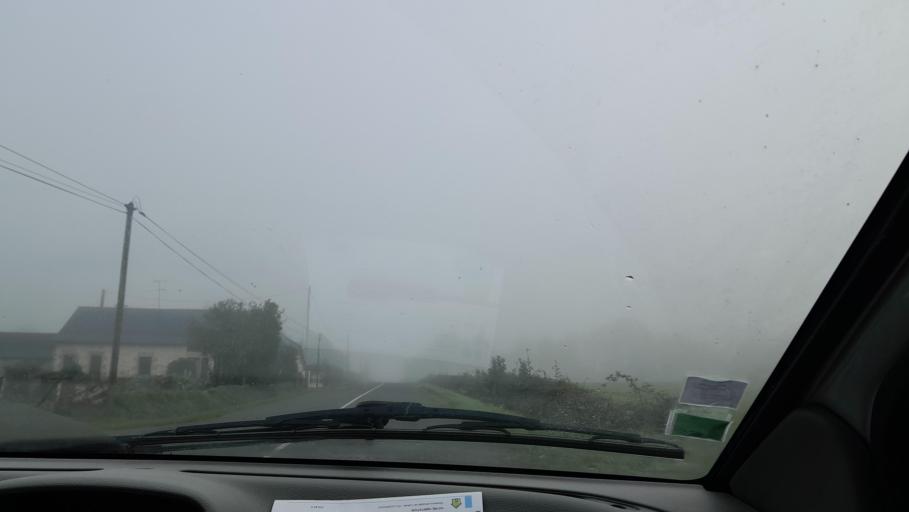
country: FR
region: Brittany
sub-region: Departement d'Ille-et-Vilaine
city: Le Pertre
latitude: 47.9731
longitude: -1.0415
